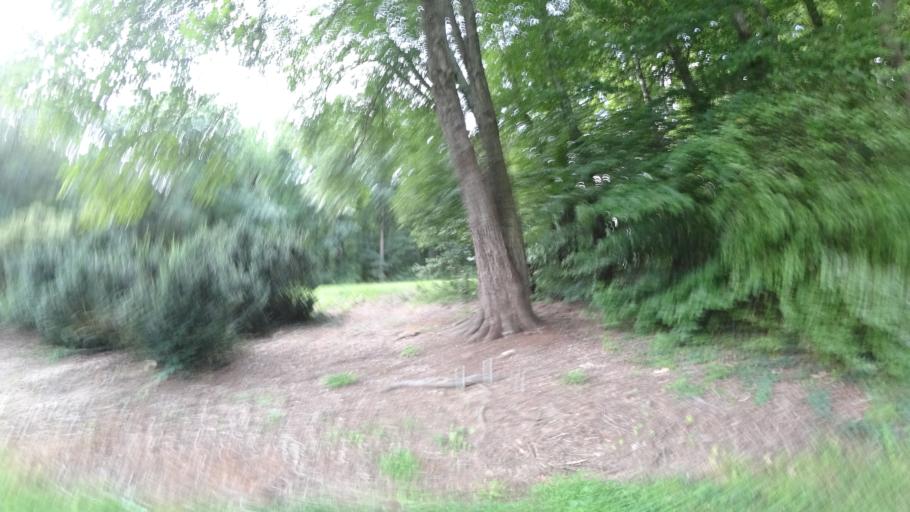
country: US
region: Maryland
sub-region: Prince George's County
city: Mount Rainier
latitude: 38.9121
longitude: -76.9737
